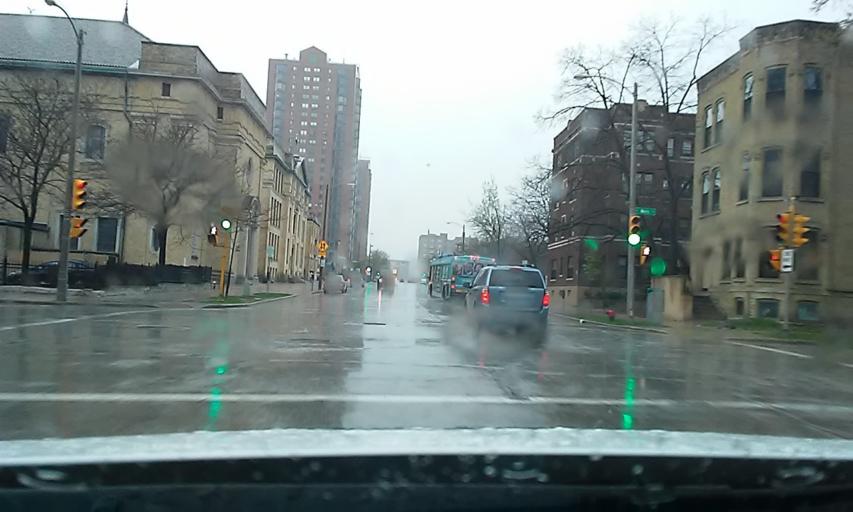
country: US
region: Wisconsin
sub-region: Milwaukee County
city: Milwaukee
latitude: 43.0412
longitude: -87.9031
